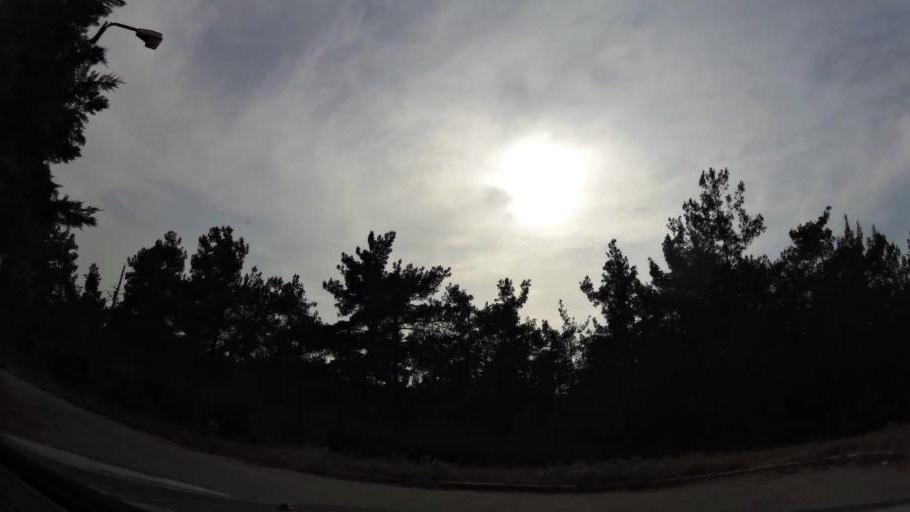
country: GR
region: Central Macedonia
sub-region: Nomos Thessalonikis
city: Oraiokastro
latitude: 40.7343
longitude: 22.9146
